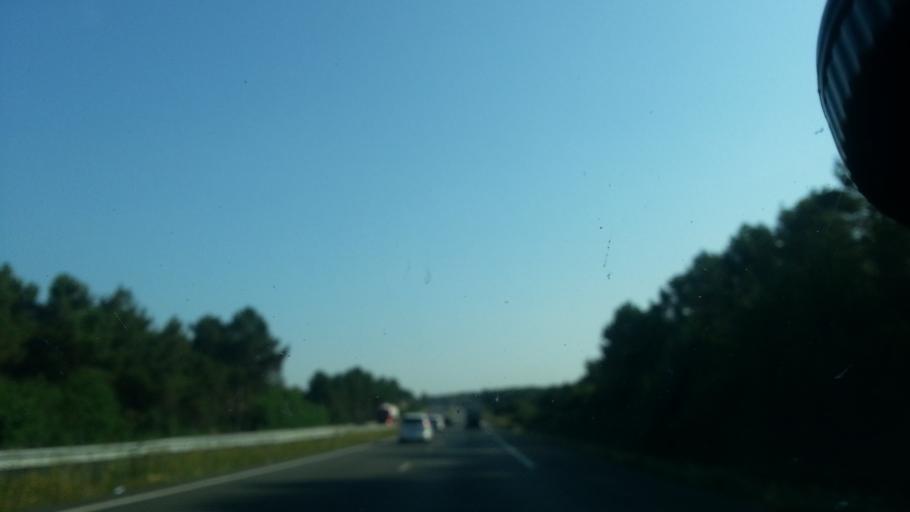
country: FR
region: Poitou-Charentes
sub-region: Departement de la Vienne
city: Dange-Saint-Romain
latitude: 46.9234
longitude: 0.5360
